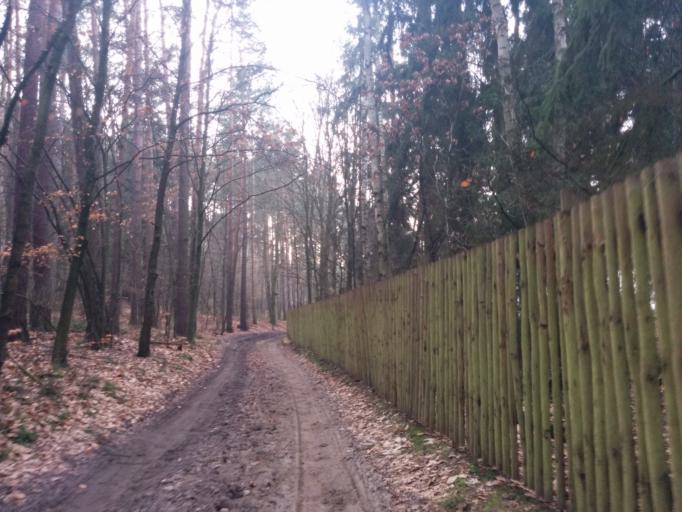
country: CZ
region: Central Bohemia
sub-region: Okres Mlada Boleslav
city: Zd'ar
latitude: 50.5288
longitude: 15.1144
